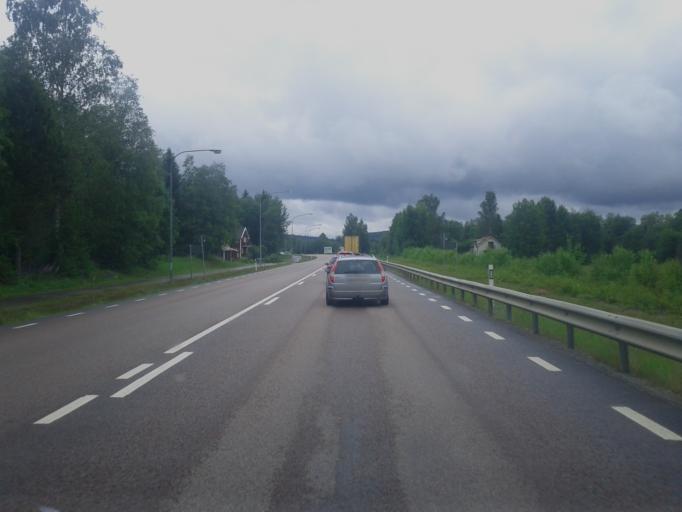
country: SE
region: Vaesternorrland
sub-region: Haernoesands Kommun
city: Haernoesand
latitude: 62.6640
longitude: 17.8533
